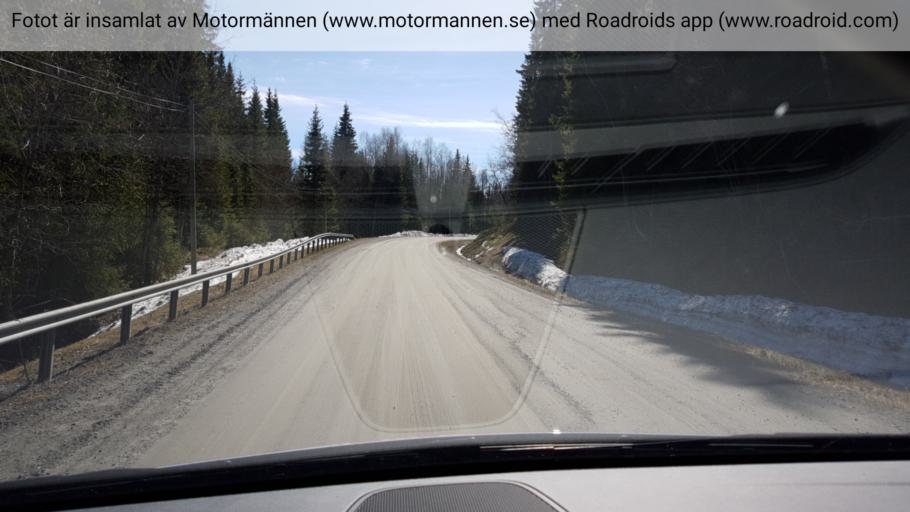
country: SE
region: Jaemtland
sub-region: Are Kommun
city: Are
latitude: 63.6915
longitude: 12.9266
